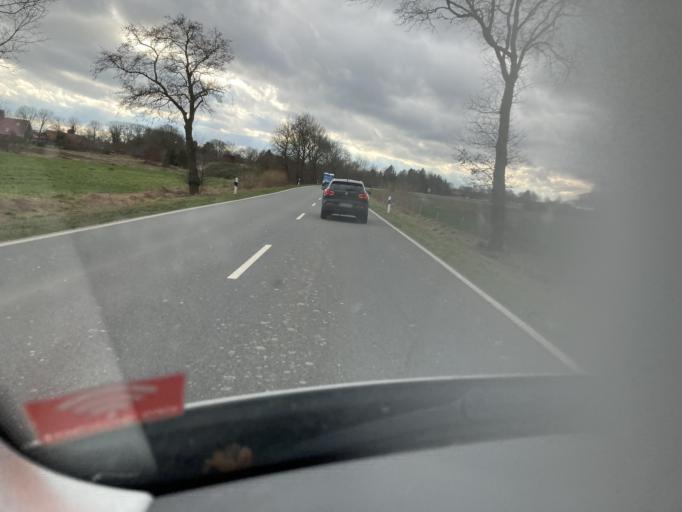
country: DE
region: Lower Saxony
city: Zetel
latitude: 53.4562
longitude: 7.9416
